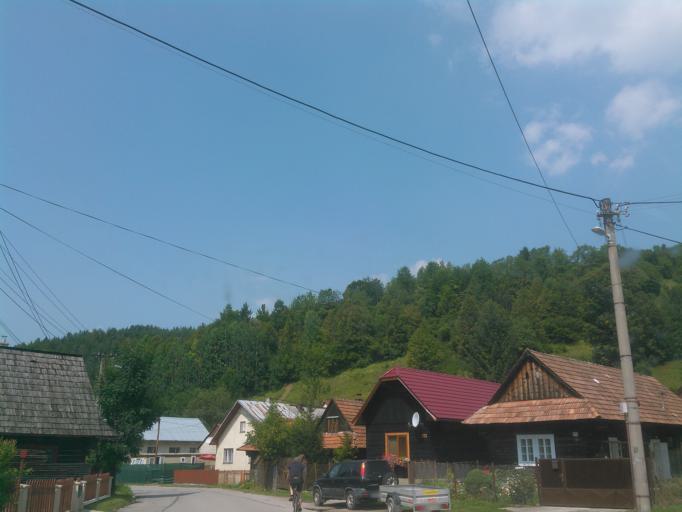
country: SK
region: Zilinsky
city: Ruzomberok
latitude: 48.9405
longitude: 19.3054
